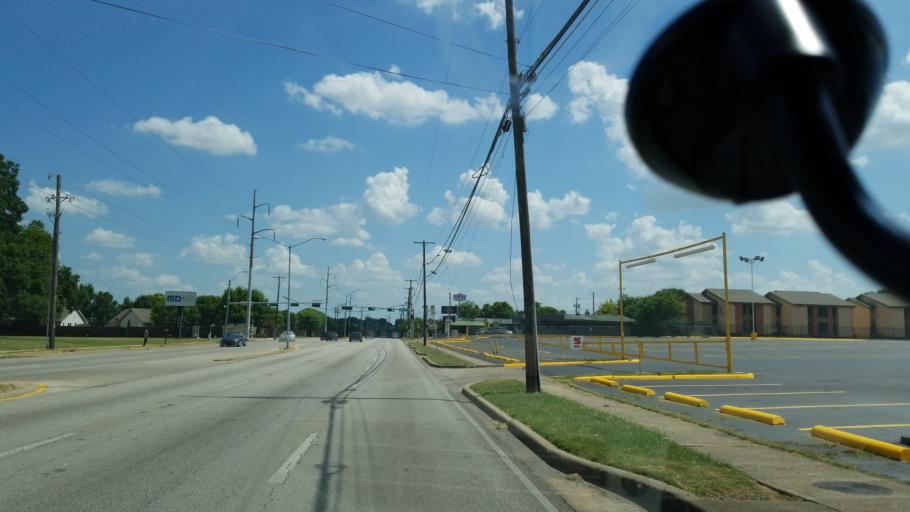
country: US
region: Texas
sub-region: Dallas County
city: Cockrell Hill
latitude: 32.7142
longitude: -96.8743
